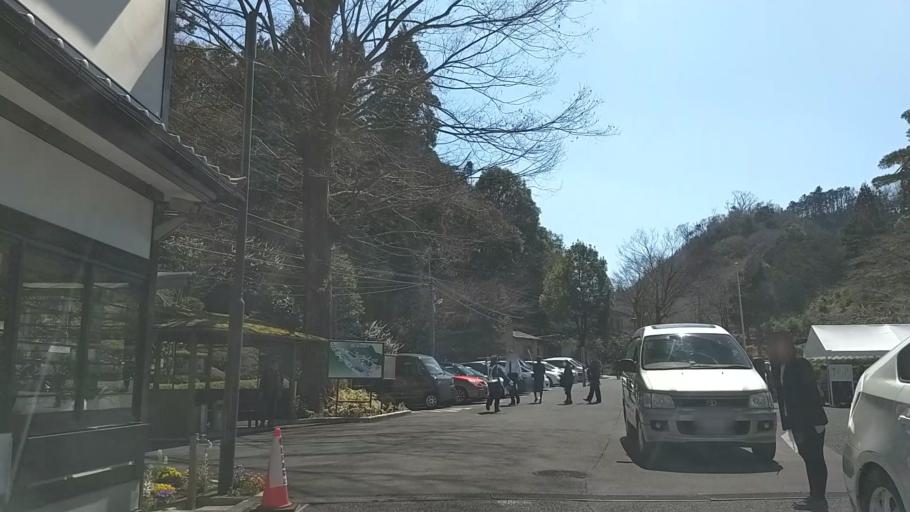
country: JP
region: Tokyo
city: Hachioji
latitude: 35.6337
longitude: 139.2762
